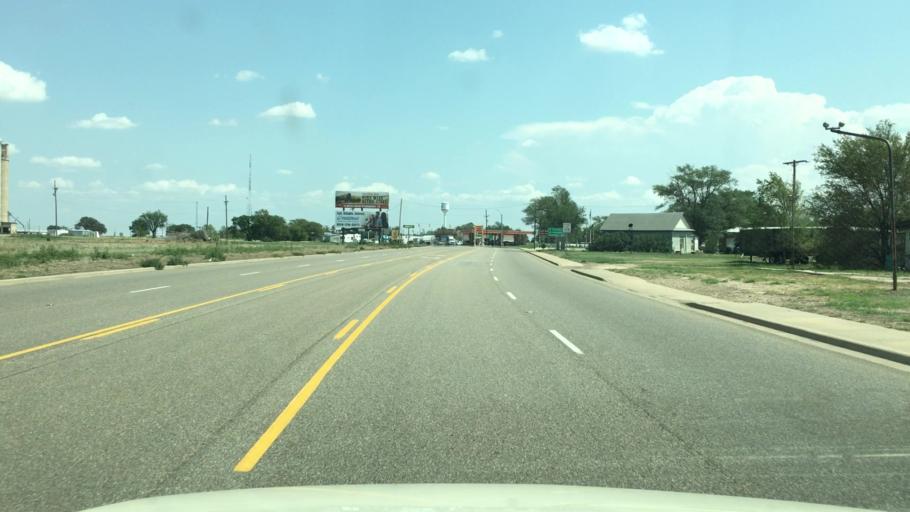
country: US
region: Texas
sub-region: Armstrong County
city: Claude
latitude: 35.1134
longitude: -101.3661
